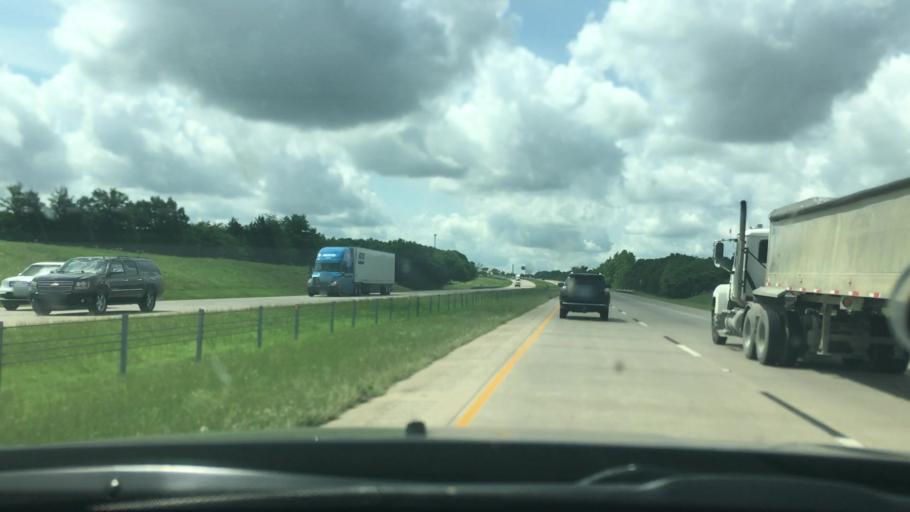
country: US
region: Oklahoma
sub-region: Love County
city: Marietta
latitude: 33.8502
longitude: -97.1343
